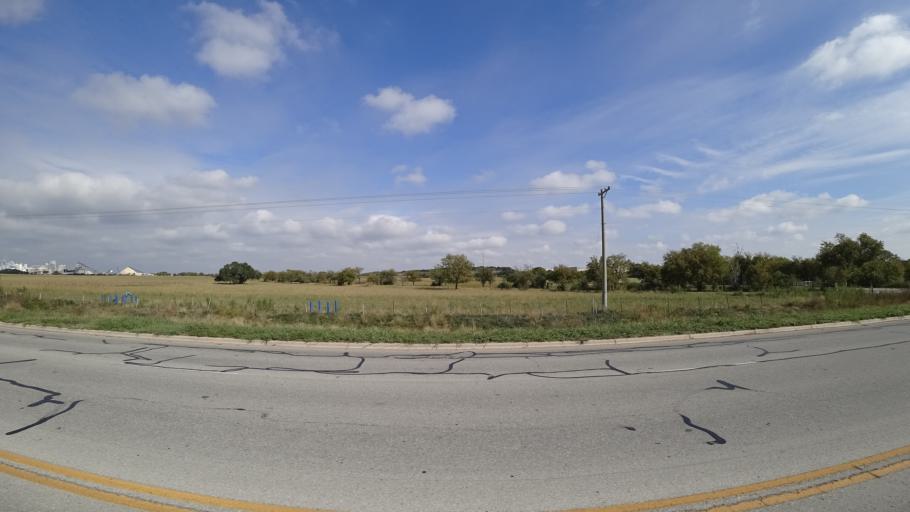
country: US
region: Texas
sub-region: Travis County
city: Wells Branch
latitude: 30.4460
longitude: -97.7133
